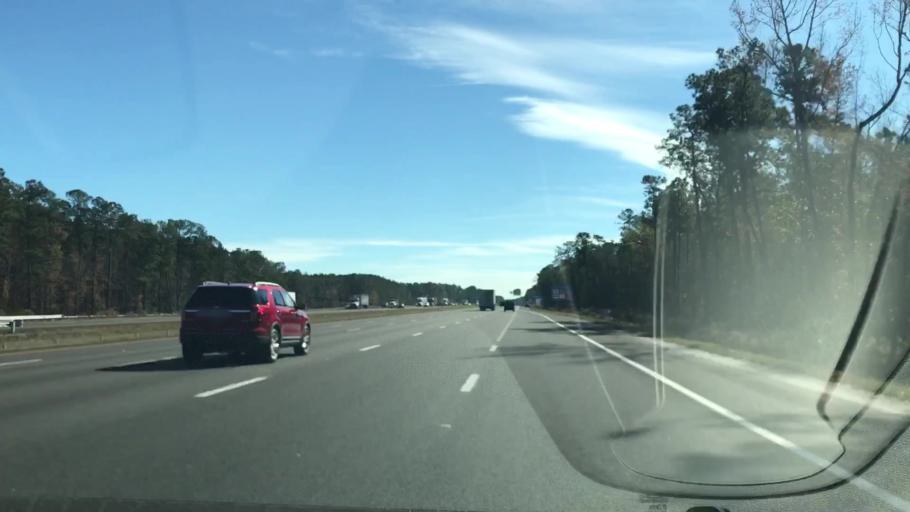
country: US
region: South Carolina
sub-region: Dorchester County
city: Summerville
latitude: 33.0497
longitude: -80.1607
